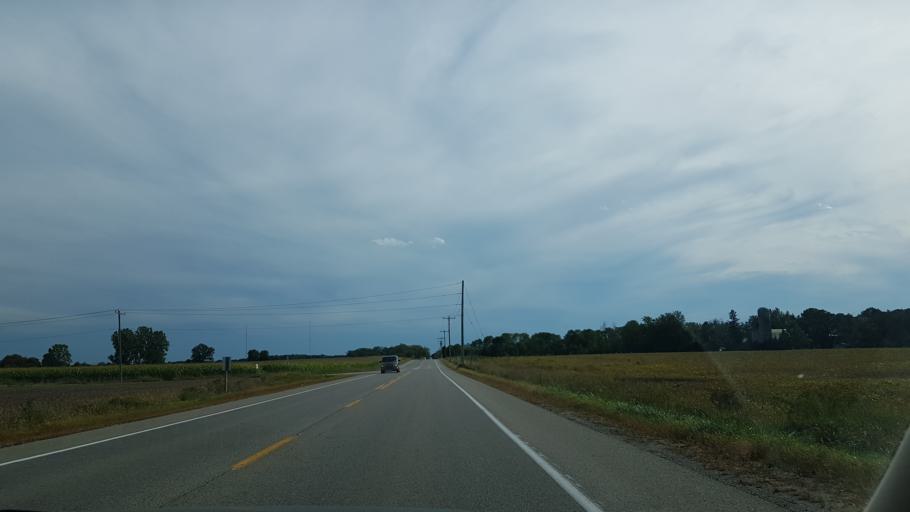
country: CA
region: Ontario
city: Delaware
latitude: 42.9953
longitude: -81.3935
